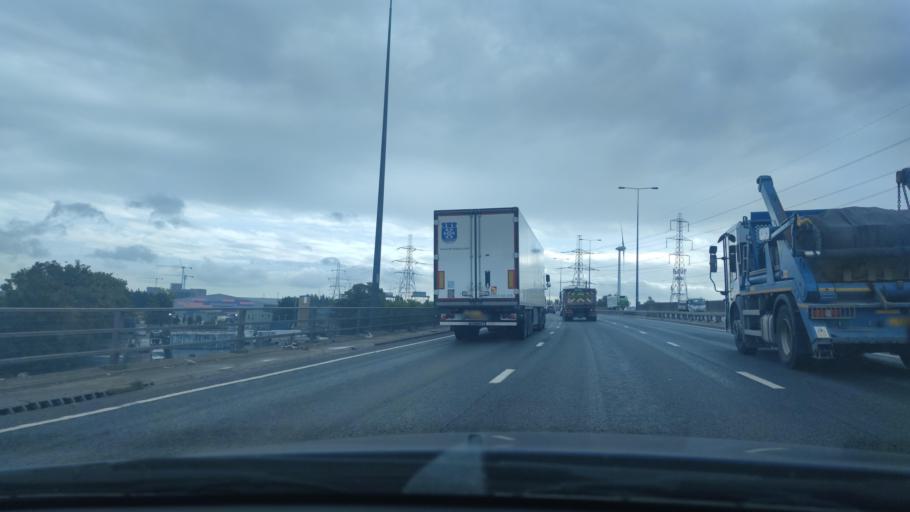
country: GB
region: England
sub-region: Greater London
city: Becontree
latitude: 51.5271
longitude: 0.1437
